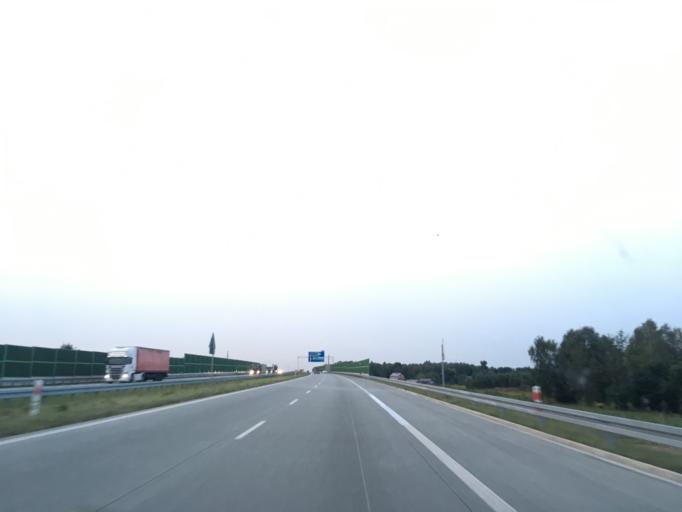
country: PL
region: Lodz Voivodeship
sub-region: Powiat lodzki wschodni
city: Andrespol
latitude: 51.7584
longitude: 19.5951
